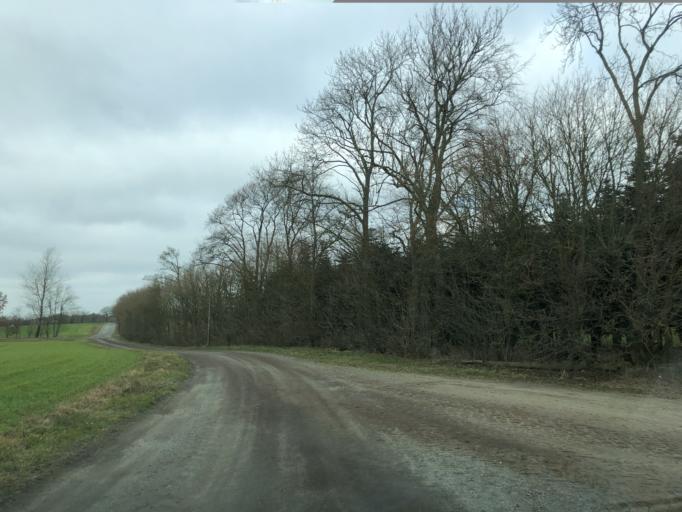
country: DK
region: South Denmark
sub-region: Billund Kommune
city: Billund
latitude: 55.7695
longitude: 9.1464
